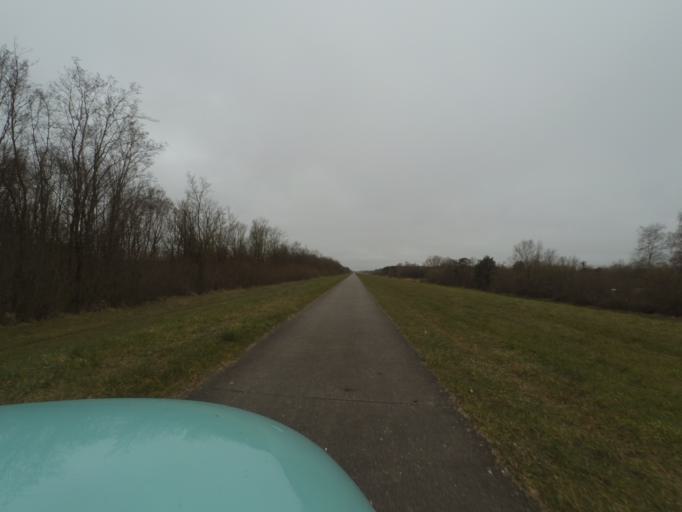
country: NL
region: Flevoland
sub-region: Gemeente Zeewolde
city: Zeewolde
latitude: 52.3099
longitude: 5.5447
